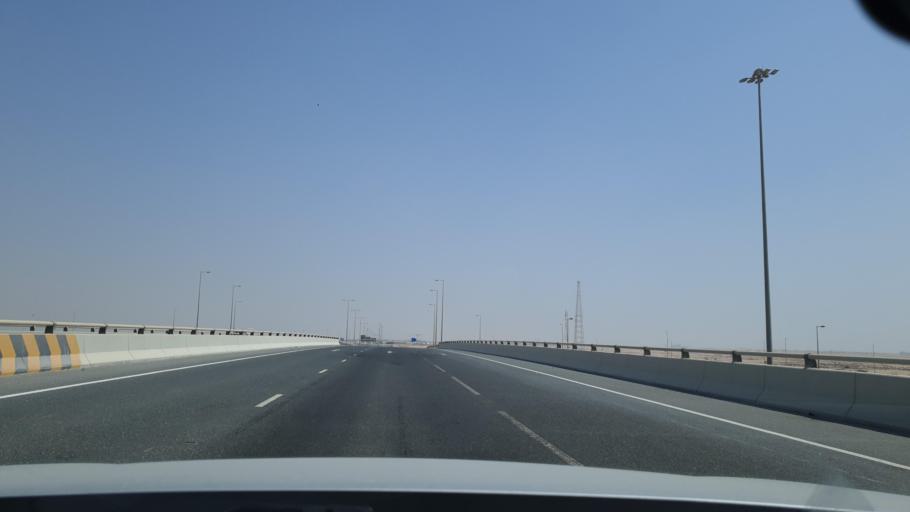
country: QA
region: Baladiyat az Za`ayin
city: Az Za`ayin
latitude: 25.6210
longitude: 51.4010
